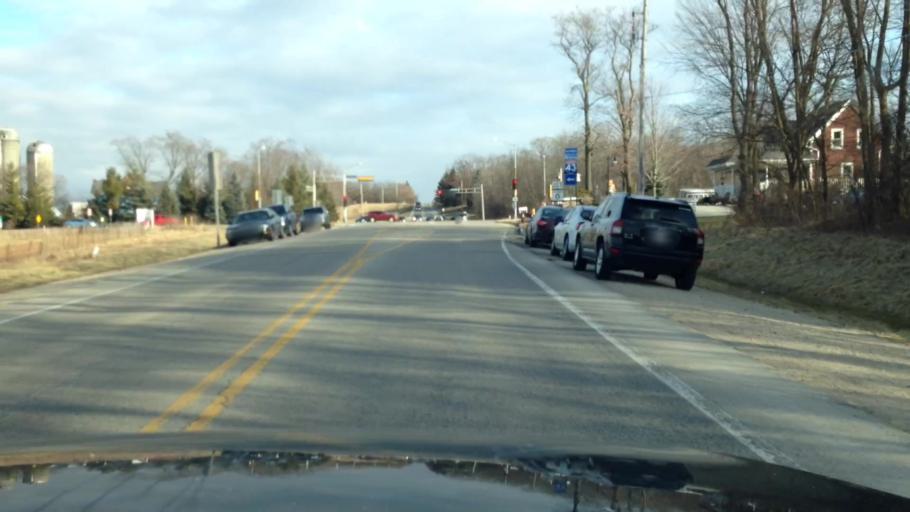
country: US
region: Wisconsin
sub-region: Waukesha County
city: Muskego
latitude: 42.9300
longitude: -88.1159
